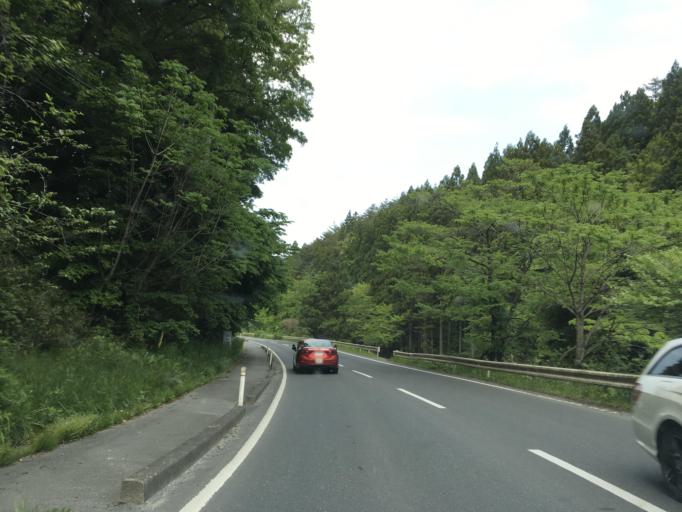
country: JP
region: Iwate
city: Ofunato
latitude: 38.8815
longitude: 141.5448
